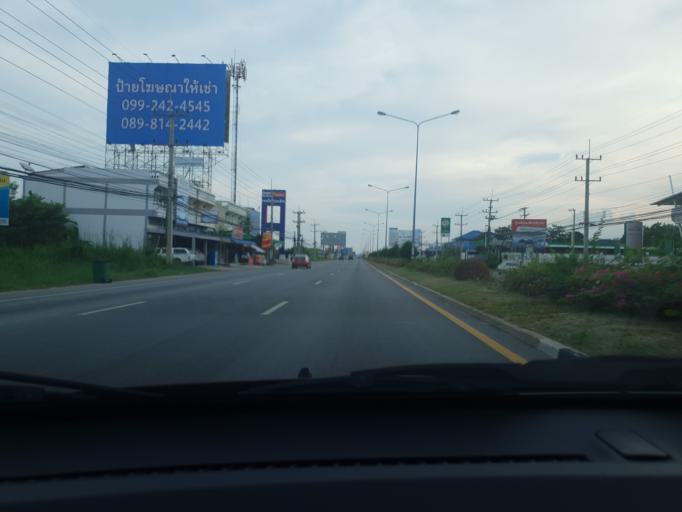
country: TH
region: Phetchaburi
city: Cha-am
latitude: 12.7781
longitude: 99.9674
